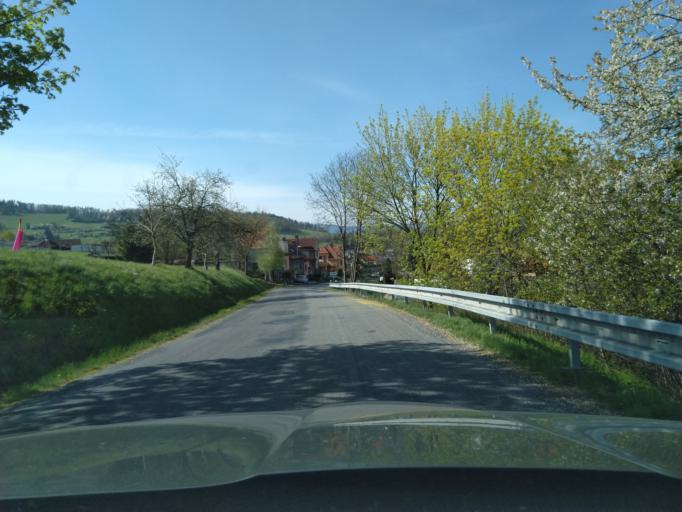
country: CZ
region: Plzensky
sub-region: Okres Klatovy
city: Susice
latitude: 49.2332
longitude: 13.5291
